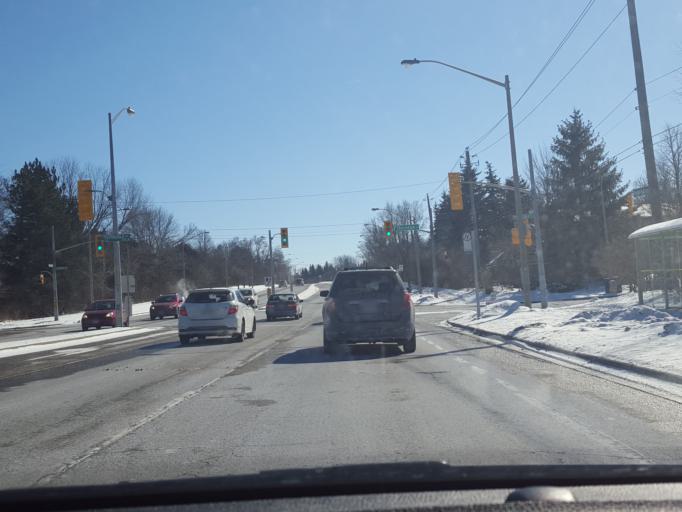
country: CA
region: Ontario
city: Waterloo
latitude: 43.4487
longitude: -80.5503
